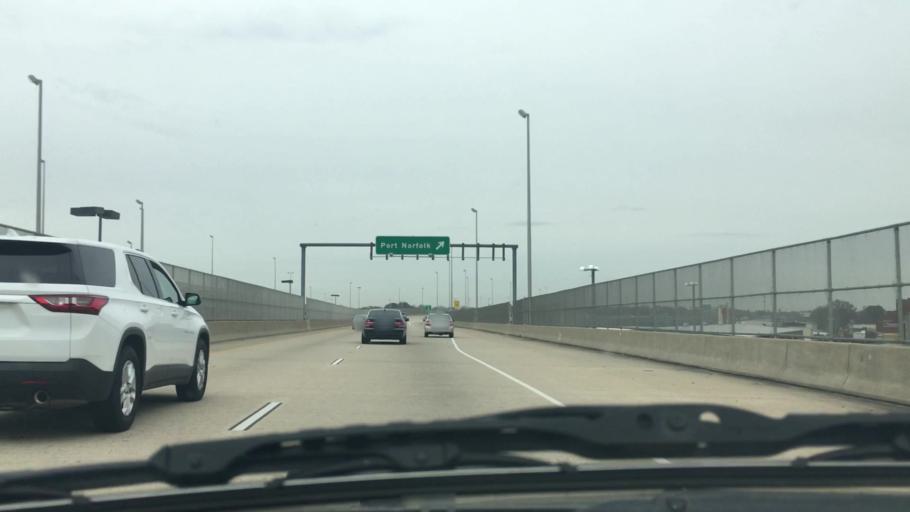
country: US
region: Virginia
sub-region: City of Portsmouth
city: Portsmouth
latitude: 36.8531
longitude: -76.3318
